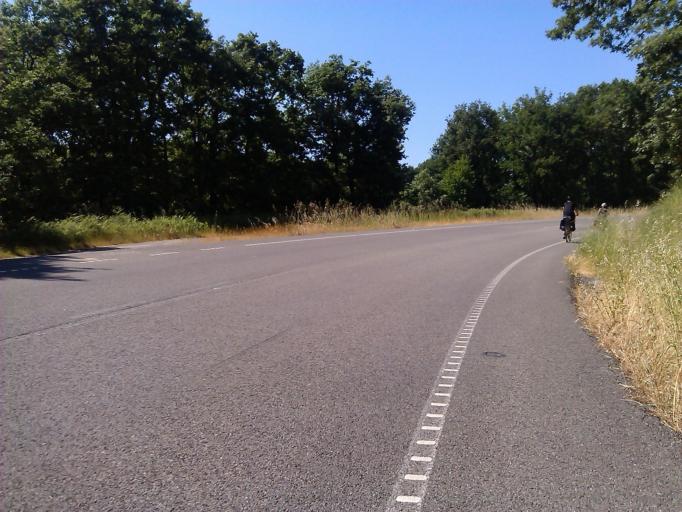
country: ES
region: Galicia
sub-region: Provincia de Lugo
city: Sarria
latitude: 42.7599
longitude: -7.3917
